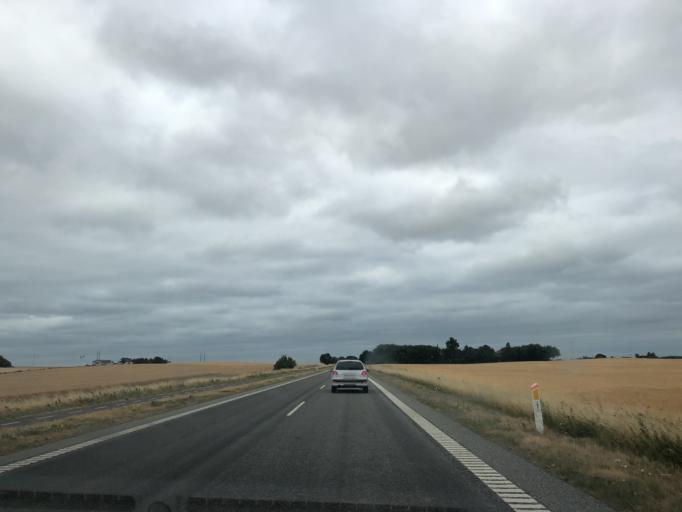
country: DK
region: Zealand
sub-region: Slagelse Kommune
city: Skaelskor
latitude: 55.2272
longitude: 11.3089
